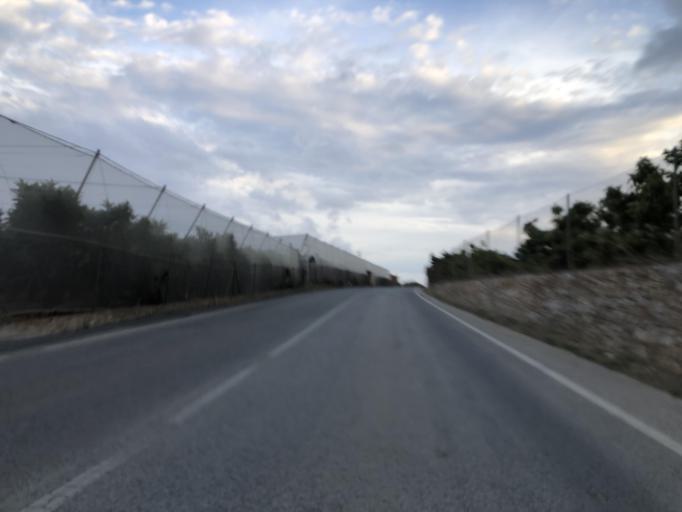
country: ES
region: Valencia
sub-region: Provincia de Alicante
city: Polop
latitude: 38.6304
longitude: -0.1423
